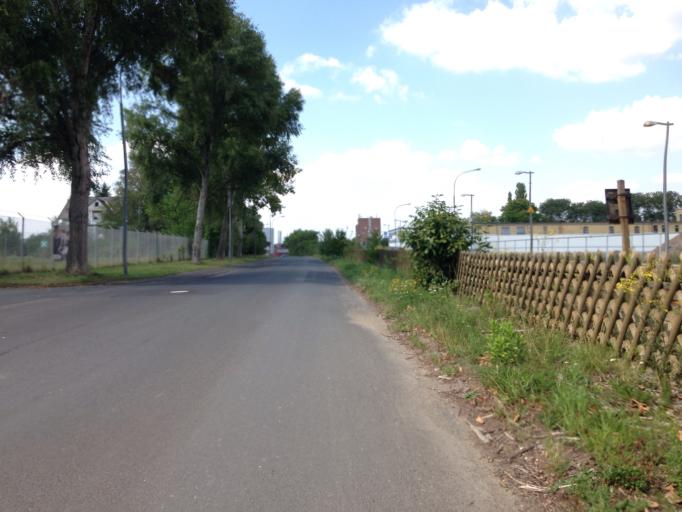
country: DE
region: Hesse
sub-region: Regierungsbezirk Giessen
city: Giessen
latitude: 50.5707
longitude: 8.6837
